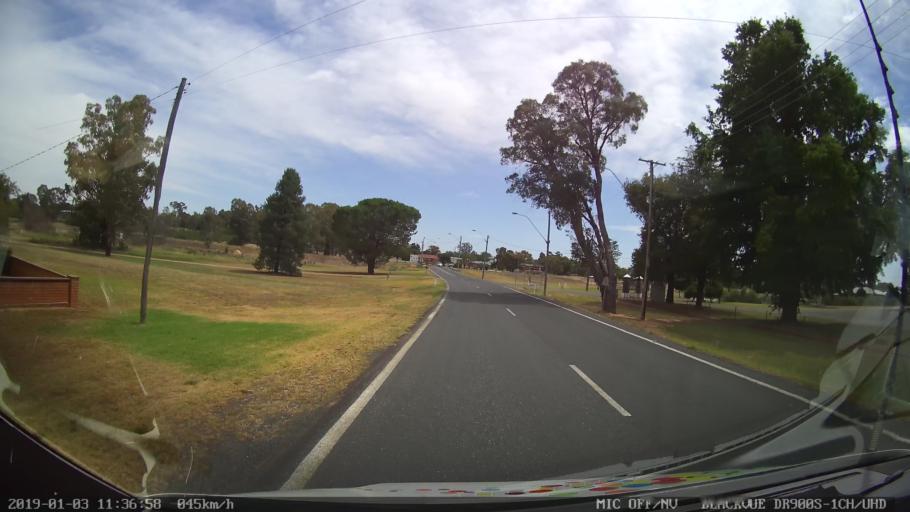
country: AU
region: New South Wales
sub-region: Weddin
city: Grenfell
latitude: -33.9060
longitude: 148.1603
